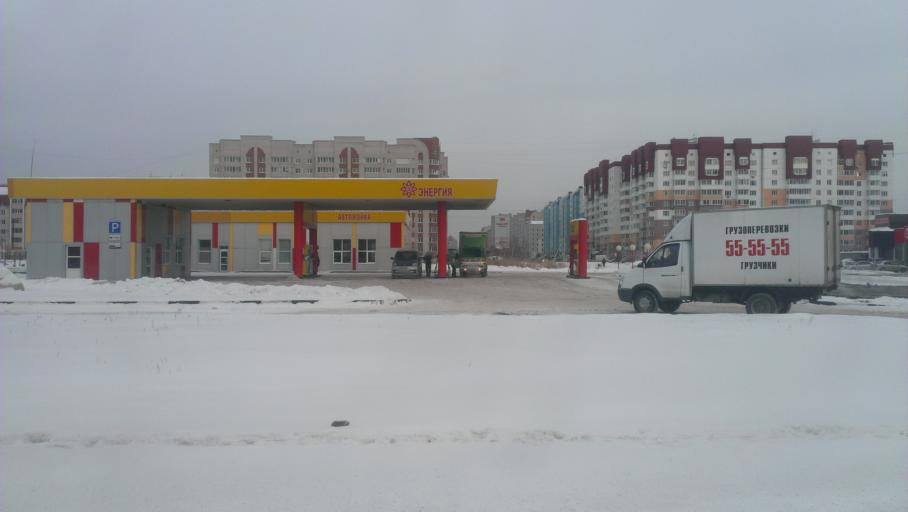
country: RU
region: Altai Krai
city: Novosilikatnyy
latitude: 53.3284
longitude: 83.6831
